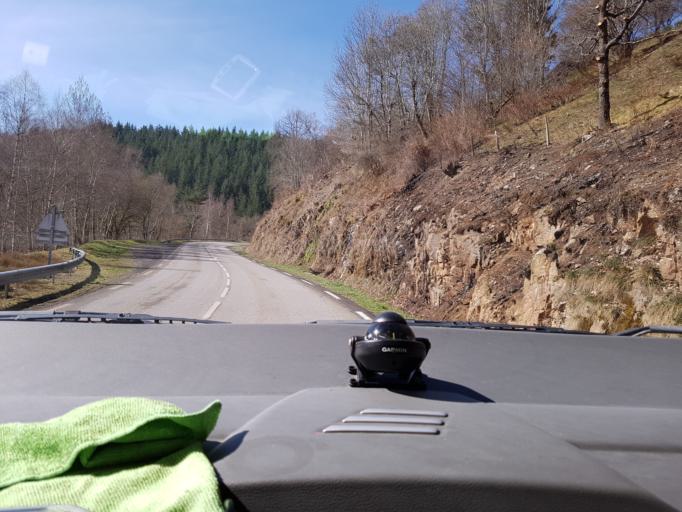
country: FR
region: Auvergne
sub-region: Departement du Cantal
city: Chaudes-Aigues
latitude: 44.8434
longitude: 3.0040
